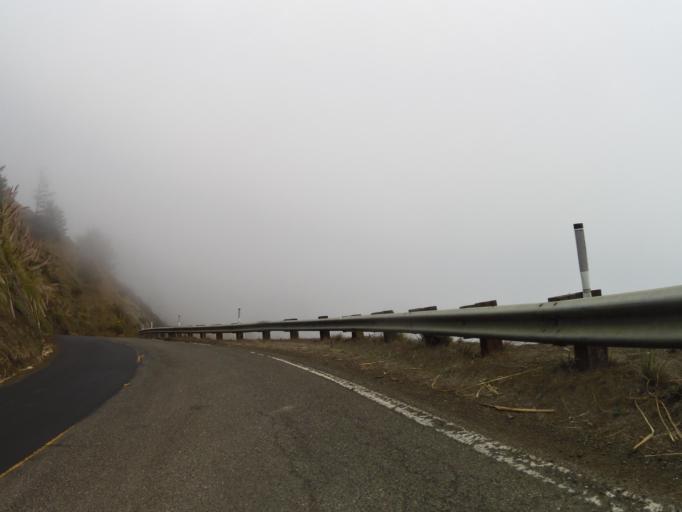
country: US
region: California
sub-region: Sonoma County
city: Monte Rio
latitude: 38.4975
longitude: -123.2047
